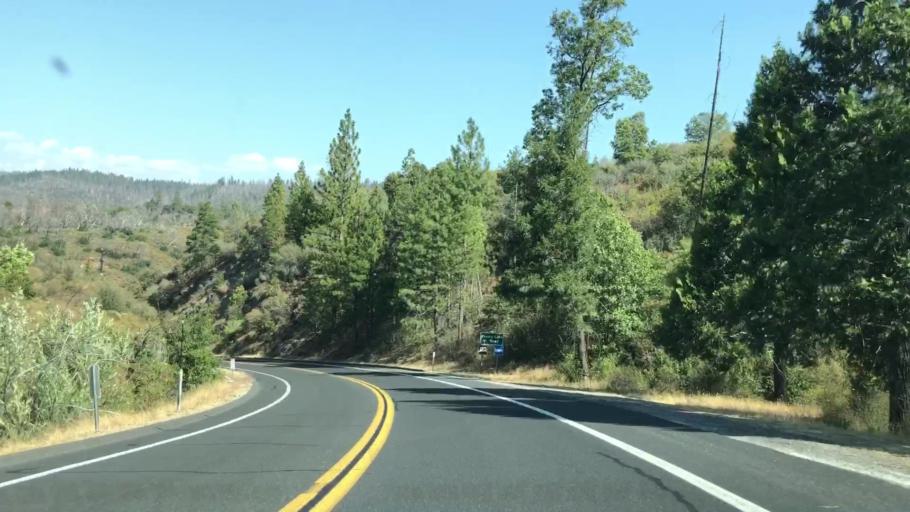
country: US
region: California
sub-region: Tuolumne County
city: Tuolumne City
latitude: 37.8226
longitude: -120.0169
